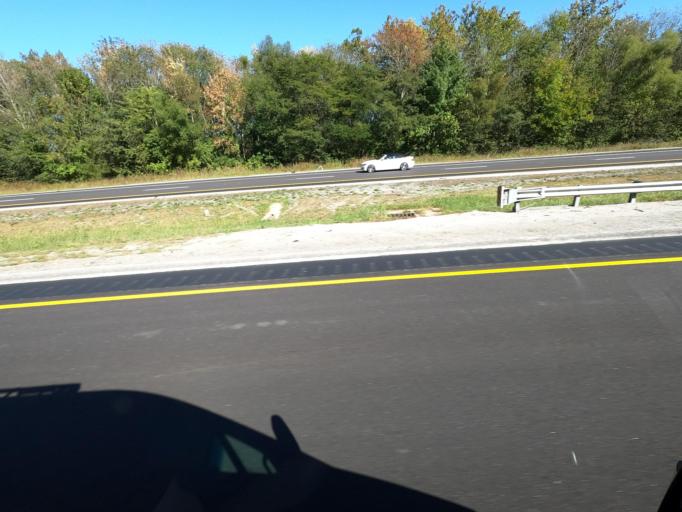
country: US
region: Tennessee
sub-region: Marion County
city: Monteagle
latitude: 35.2926
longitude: -85.8978
